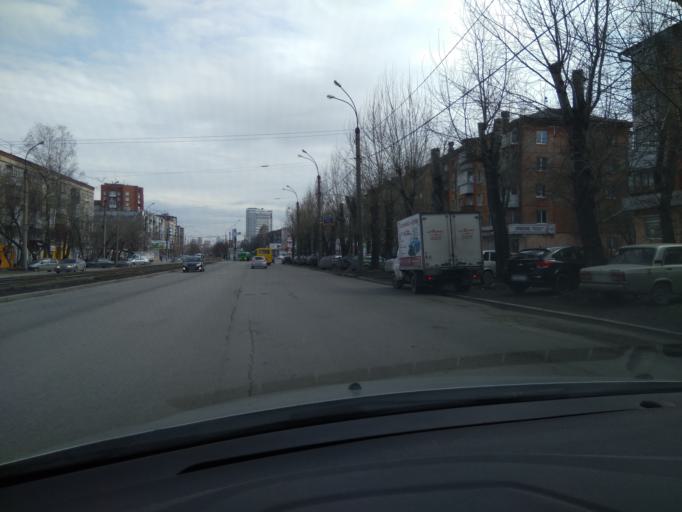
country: RU
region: Sverdlovsk
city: Shuvakish
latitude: 56.8671
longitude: 60.5299
